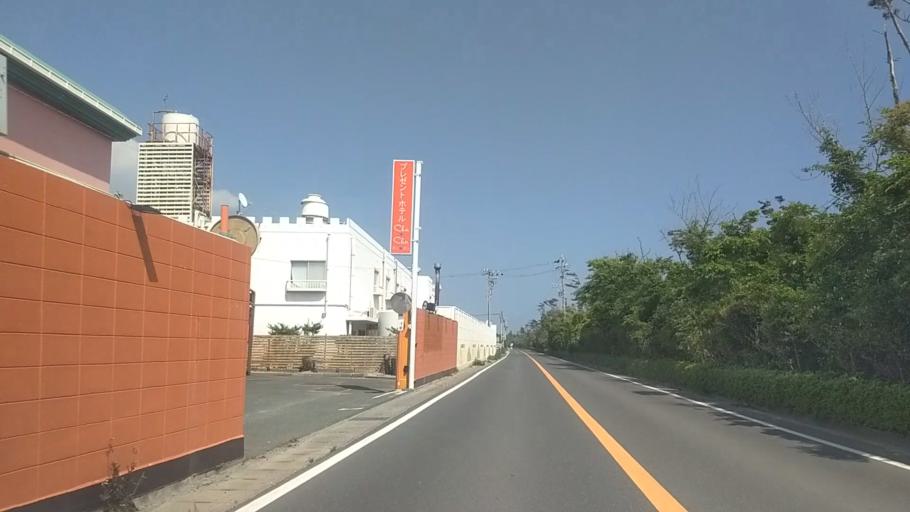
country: JP
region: Shizuoka
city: Hamamatsu
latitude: 34.6698
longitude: 137.6948
